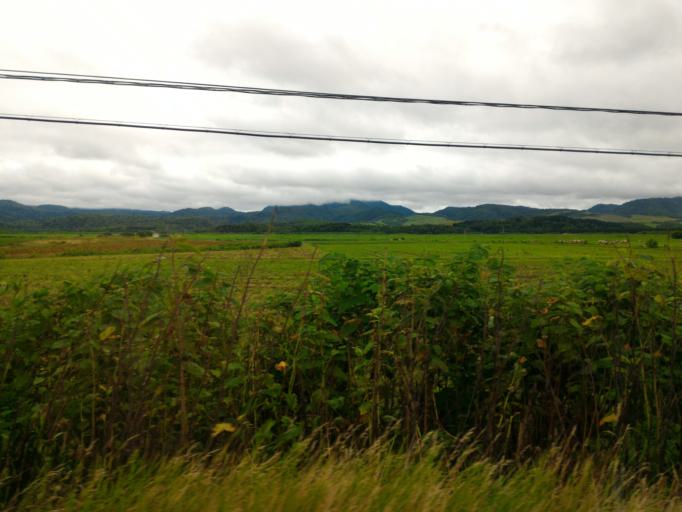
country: JP
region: Hokkaido
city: Makubetsu
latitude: 44.8290
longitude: 142.0608
